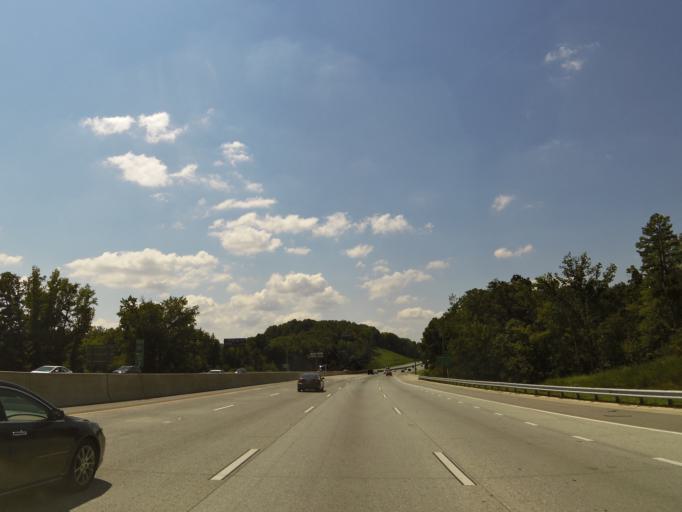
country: US
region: North Carolina
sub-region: Cabarrus County
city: Harrisburg
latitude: 35.4135
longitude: -80.6784
